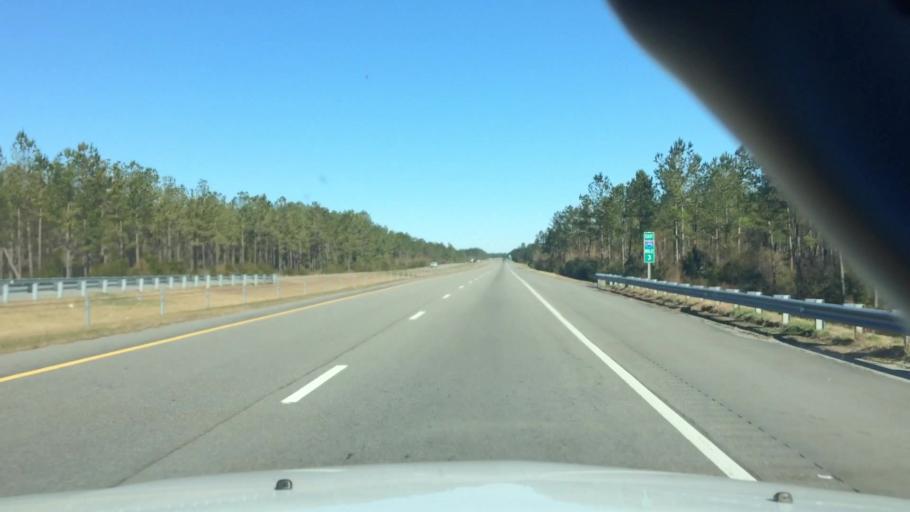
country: US
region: North Carolina
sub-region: Brunswick County
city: Leland
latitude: 34.2189
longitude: -78.0768
